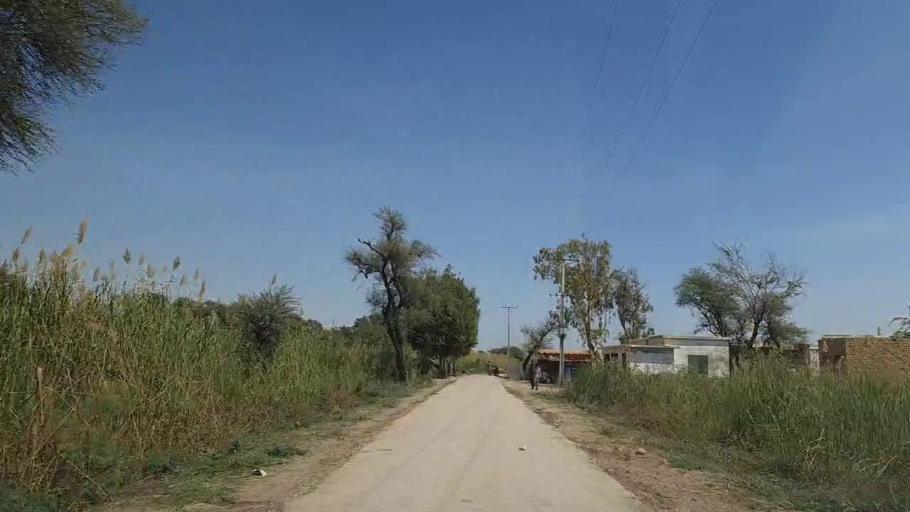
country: PK
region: Sindh
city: Thatta
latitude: 24.7865
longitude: 67.7545
